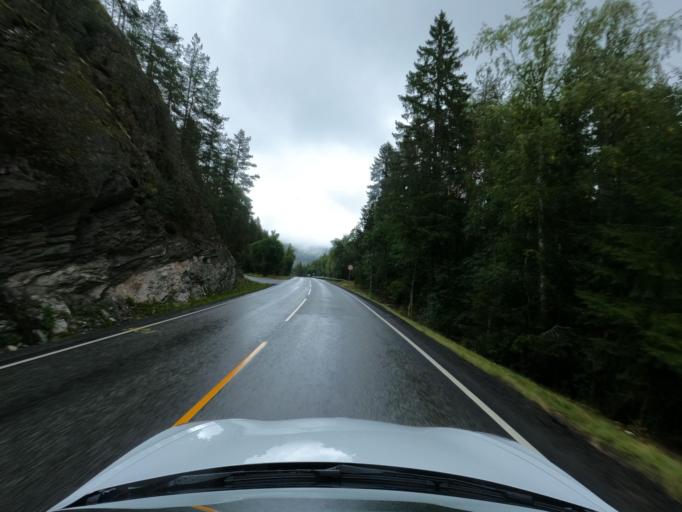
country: NO
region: Telemark
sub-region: Kviteseid
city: Kviteseid
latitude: 59.4455
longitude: 8.5503
